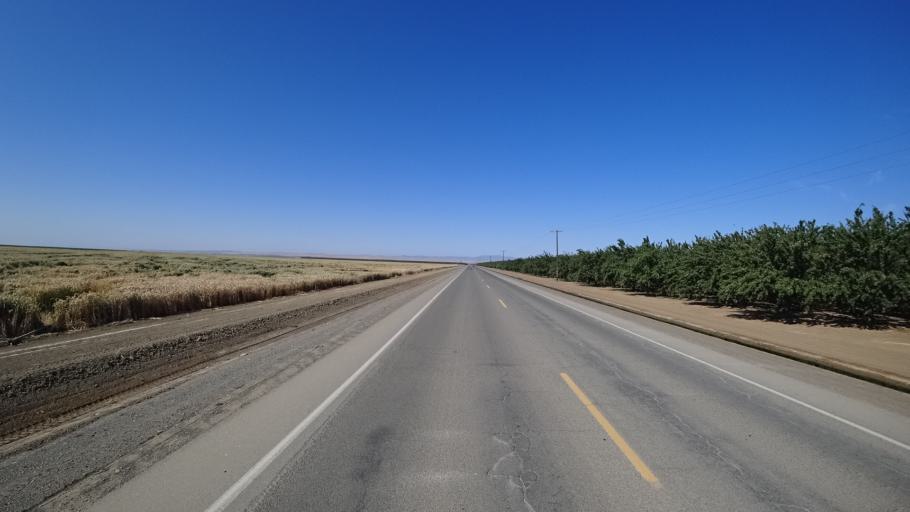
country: US
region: California
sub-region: Kings County
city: Lemoore Station
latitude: 36.1710
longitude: -119.9689
